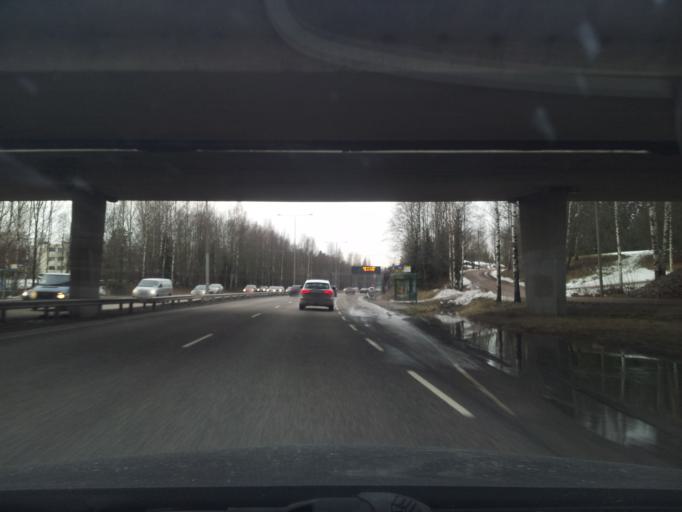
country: FI
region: Uusimaa
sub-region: Helsinki
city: Teekkarikylae
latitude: 60.2306
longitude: 24.8477
